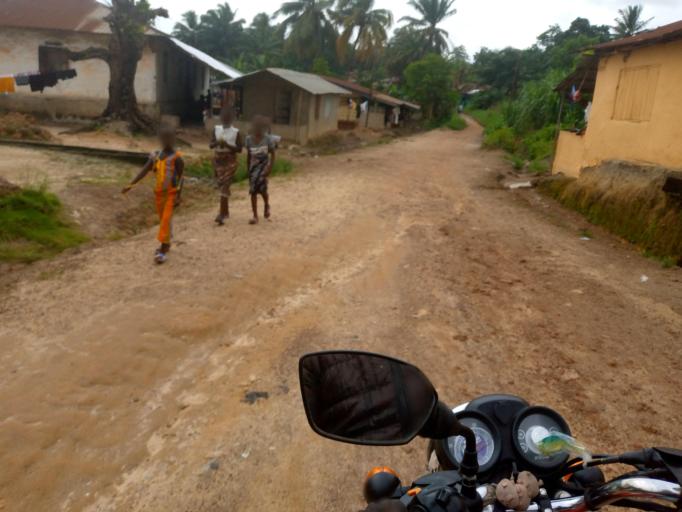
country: SL
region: Eastern Province
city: Kenema
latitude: 7.8774
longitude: -11.1812
